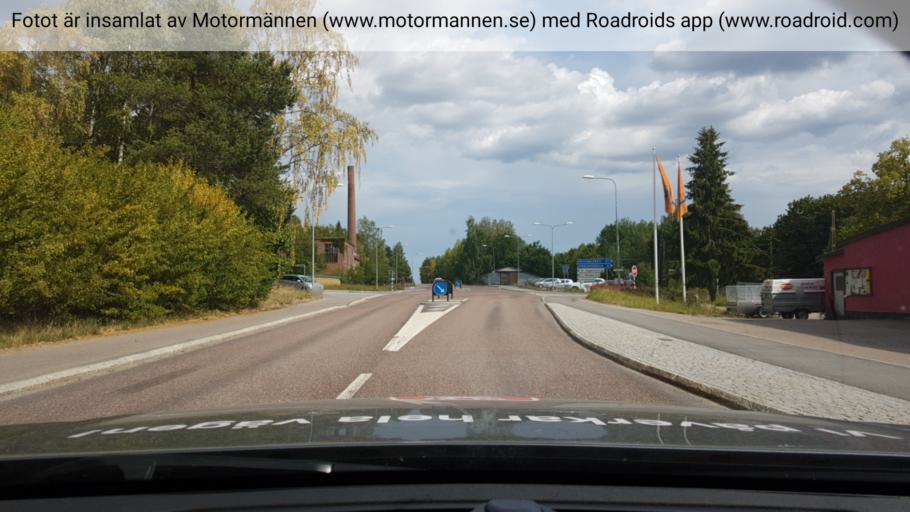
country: SE
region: Uppsala
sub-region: Enkopings Kommun
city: Orsundsbro
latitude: 59.8865
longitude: 17.1968
